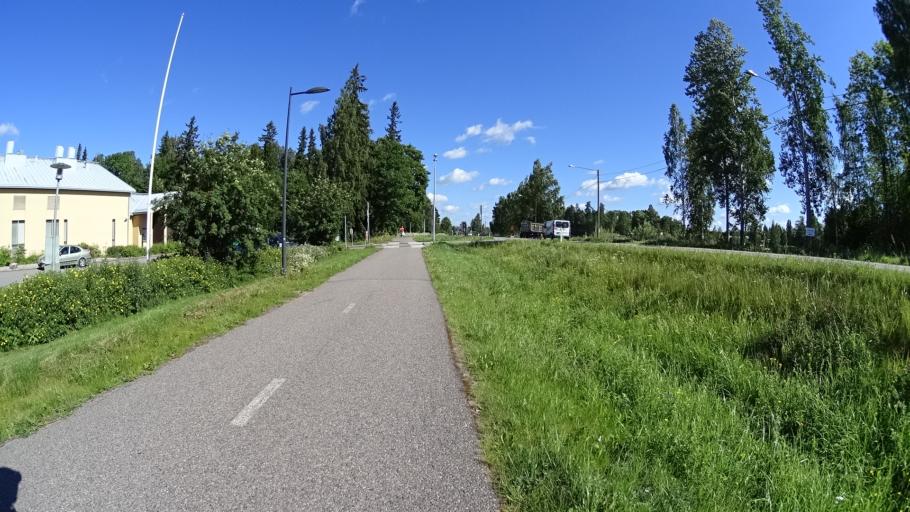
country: FI
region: Uusimaa
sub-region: Helsinki
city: Jaervenpaeae
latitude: 60.4581
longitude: 25.0843
